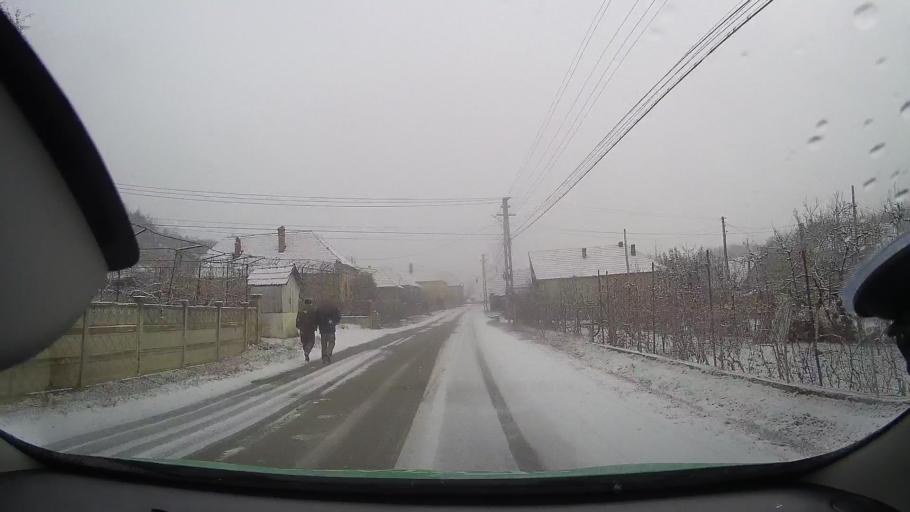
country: RO
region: Alba
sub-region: Comuna Livezile
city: Livezile
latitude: 46.3489
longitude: 23.6329
